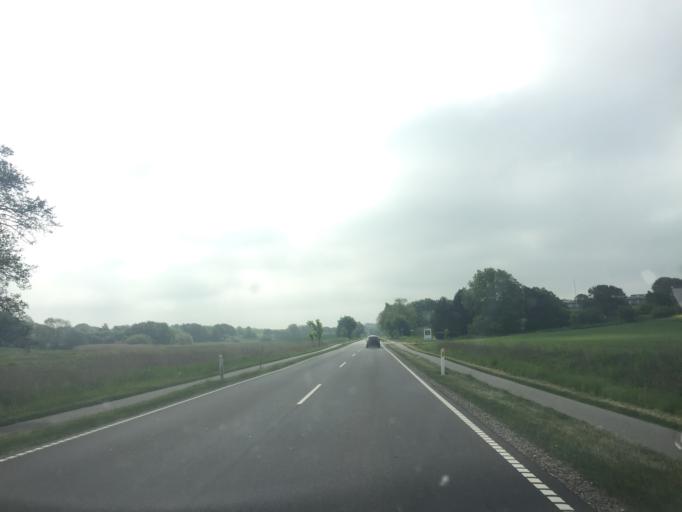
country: DK
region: South Denmark
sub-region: Kolding Kommune
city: Sonder Bjert
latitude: 55.4696
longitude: 9.5303
